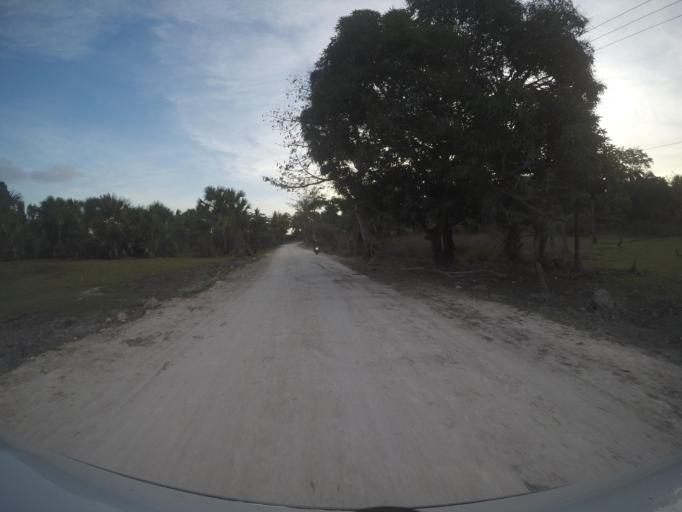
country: TL
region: Viqueque
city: Viqueque
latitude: -8.9396
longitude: 126.4421
